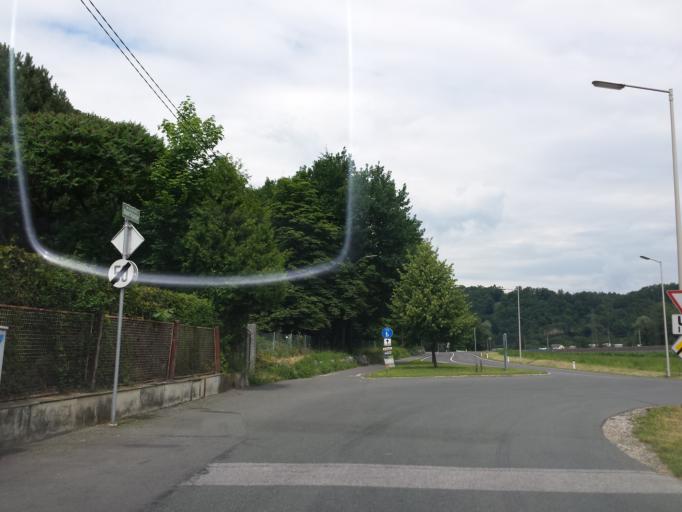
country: AT
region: Styria
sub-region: Politischer Bezirk Graz-Umgebung
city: Gratkorn
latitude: 47.1150
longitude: 15.3707
